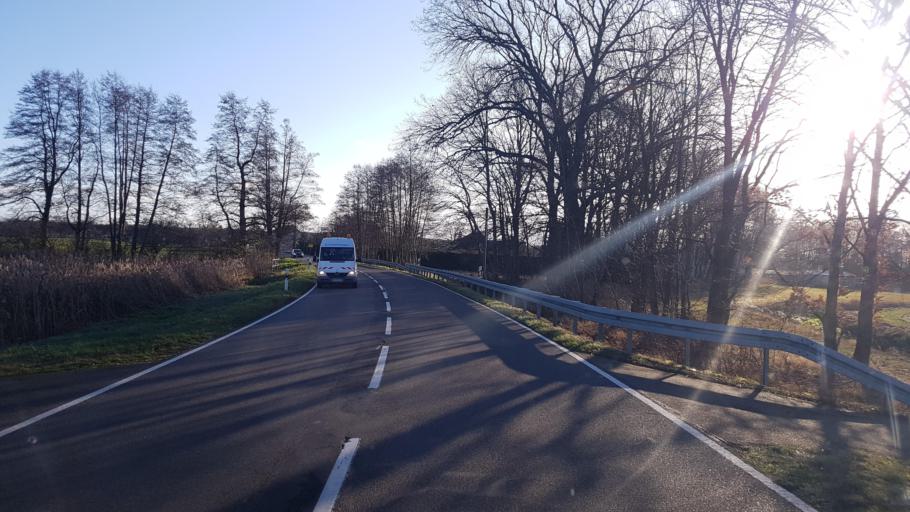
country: DE
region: Brandenburg
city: Heinersbruck
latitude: 51.7270
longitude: 14.4762
